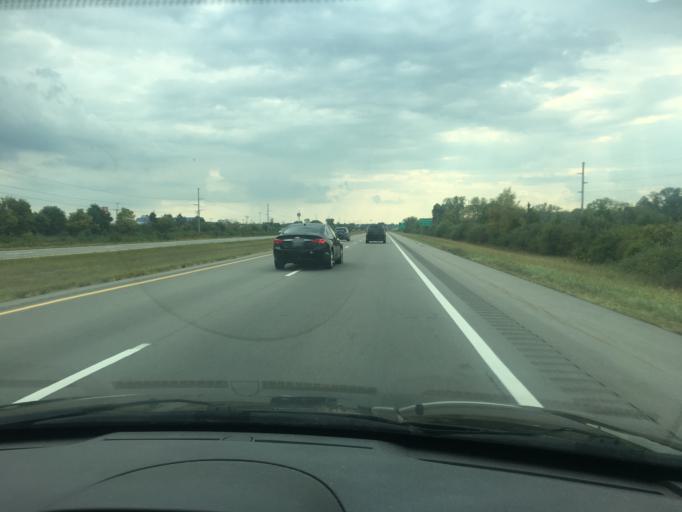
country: US
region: Ohio
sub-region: Clark County
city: Springfield
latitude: 39.9538
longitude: -83.8310
